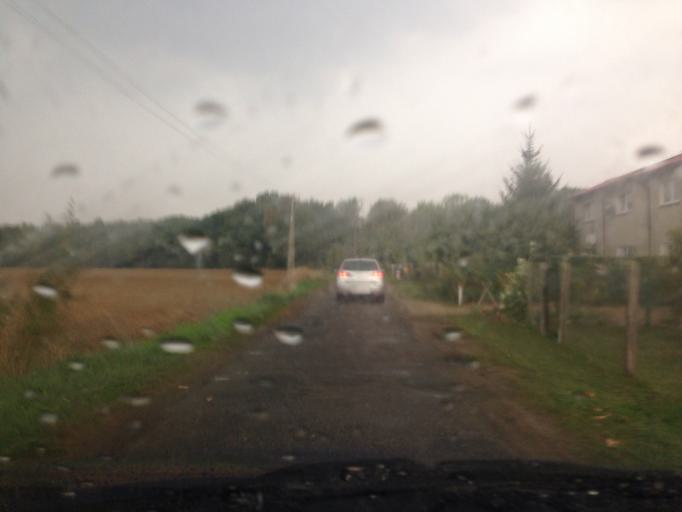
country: PL
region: Kujawsko-Pomorskie
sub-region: Powiat swiecki
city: Warlubie
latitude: 53.4736
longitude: 18.6378
